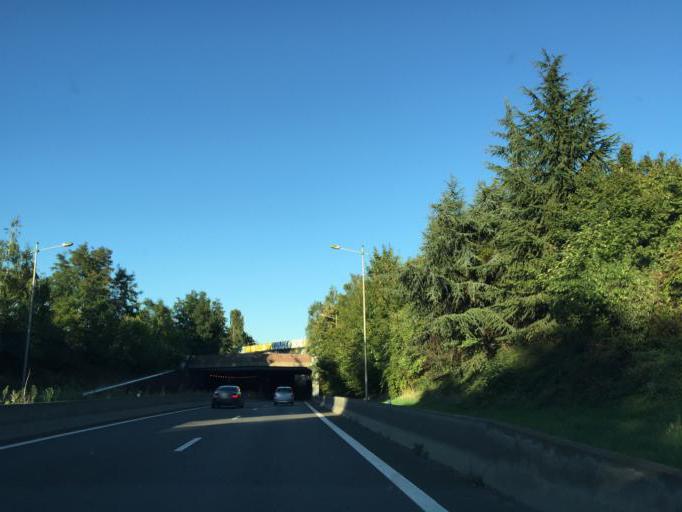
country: FR
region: Rhone-Alpes
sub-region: Departement de la Loire
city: Unieux
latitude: 45.3889
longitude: 4.2788
